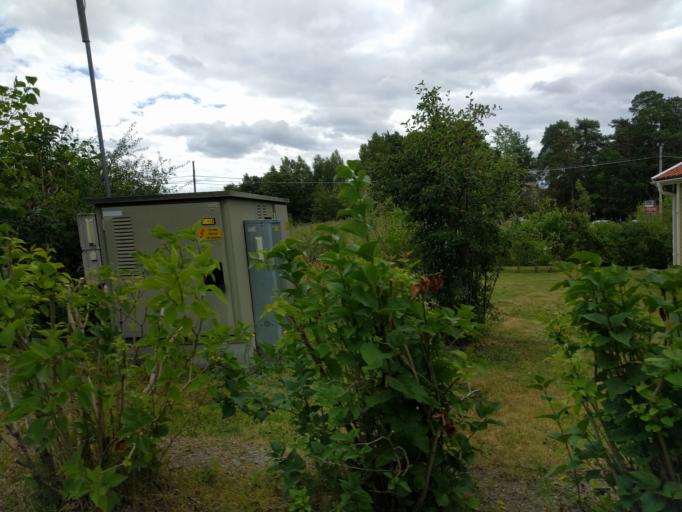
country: SE
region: Soedermanland
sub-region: Oxelosunds Kommun
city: Bara
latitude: 58.4928
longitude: 16.9344
